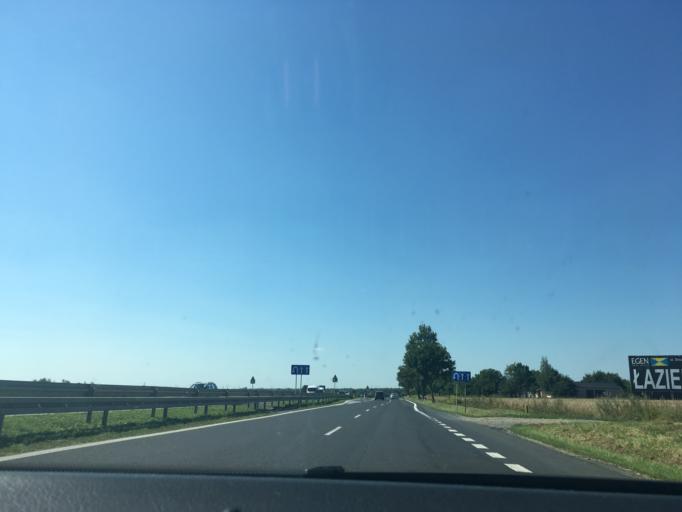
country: PL
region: Lublin Voivodeship
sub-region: Powiat lubelski
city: Niemce
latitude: 51.3311
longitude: 22.6146
